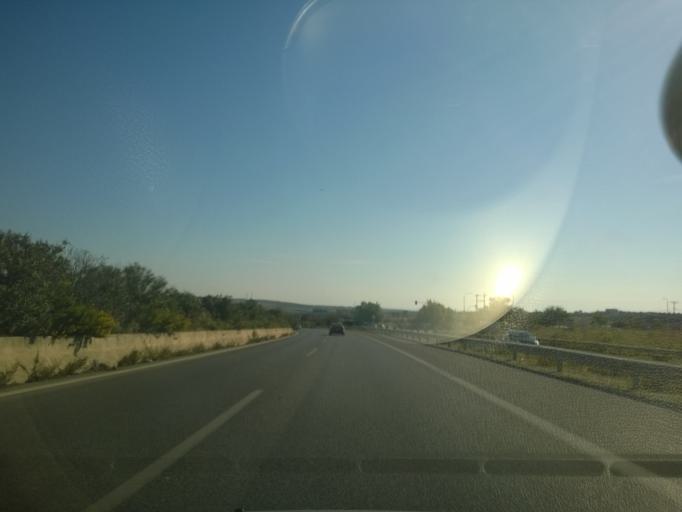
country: GR
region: Central Macedonia
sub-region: Nomos Thessalonikis
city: Mesimeri
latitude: 40.4146
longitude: 23.0228
